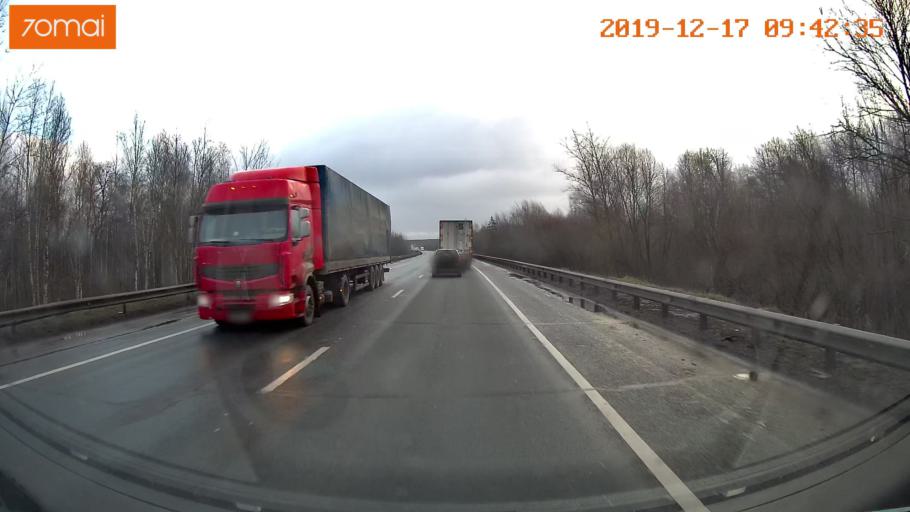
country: RU
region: Vladimir
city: Raduzhnyy
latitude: 56.0593
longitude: 40.3823
